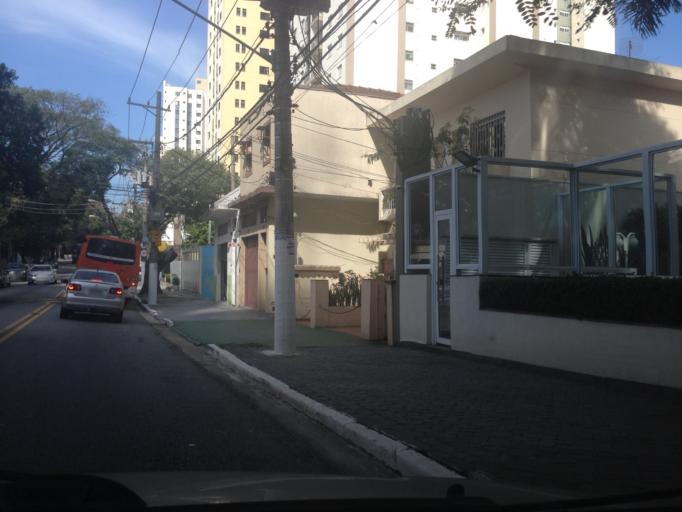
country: BR
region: Sao Paulo
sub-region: Sao Paulo
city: Sao Paulo
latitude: -23.5303
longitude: -46.7045
